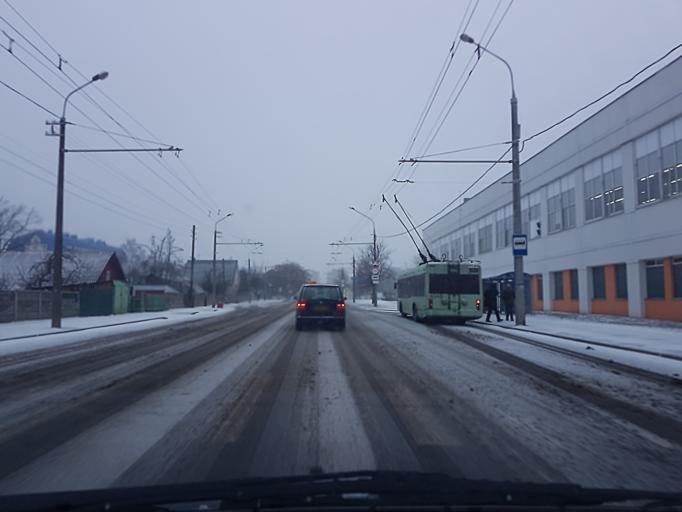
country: BY
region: Minsk
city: Minsk
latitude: 53.9045
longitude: 27.5135
